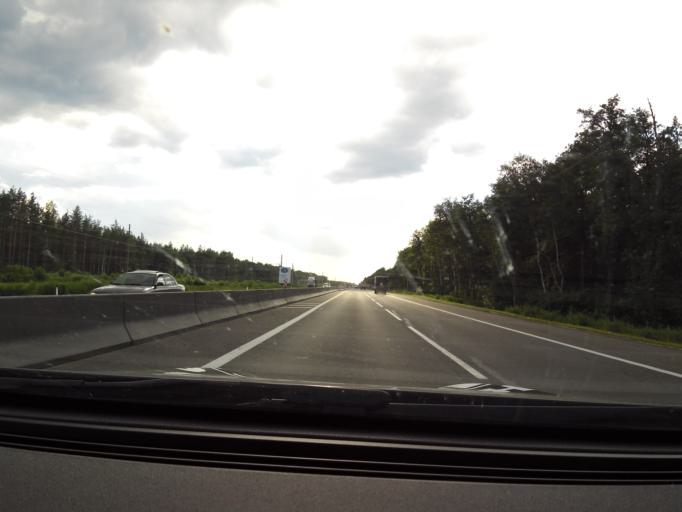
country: RU
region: Nizjnij Novgorod
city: Volodarsk
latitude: 56.2848
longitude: 43.1601
